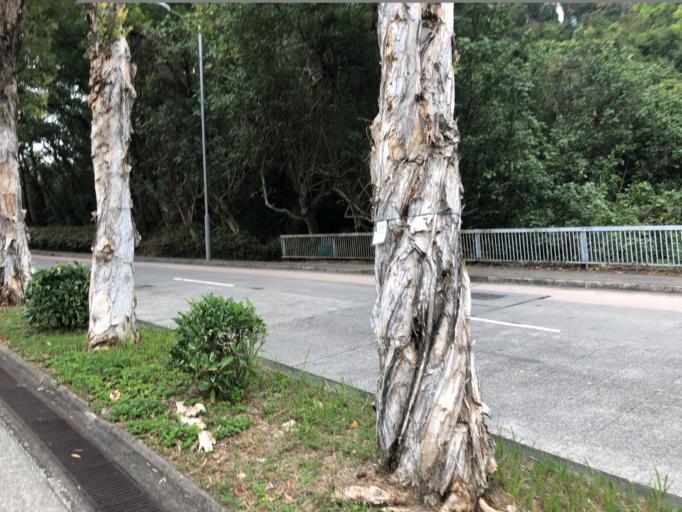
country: HK
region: Tai Po
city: Tai Po
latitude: 22.4641
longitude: 114.1930
